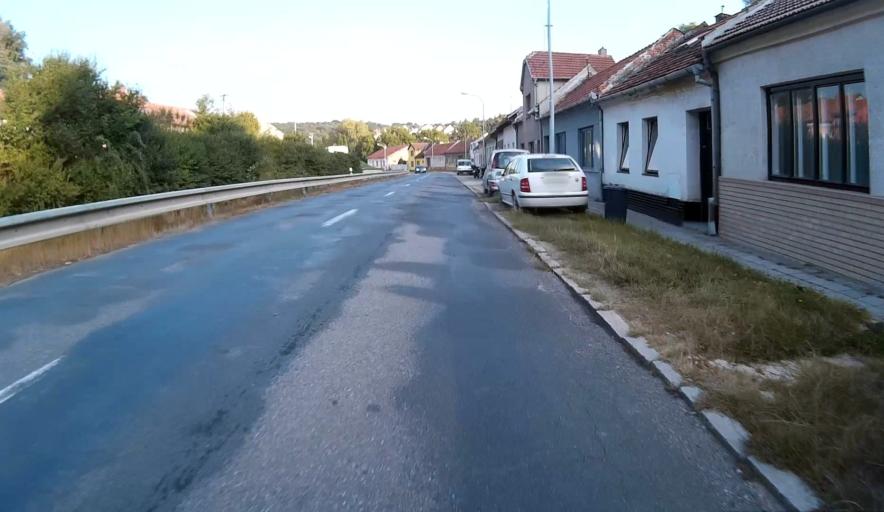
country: CZ
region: South Moravian
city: Podoli
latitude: 49.2038
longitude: 16.7092
